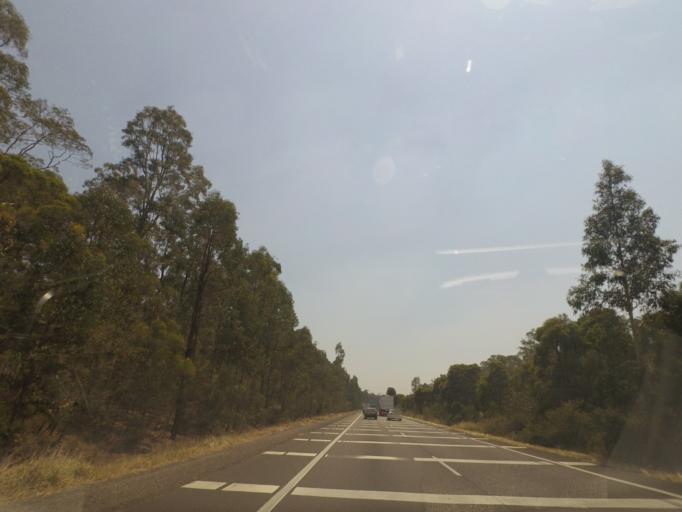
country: AU
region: New South Wales
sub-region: Newcastle
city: Beresfield
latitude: -32.8227
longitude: 151.6337
